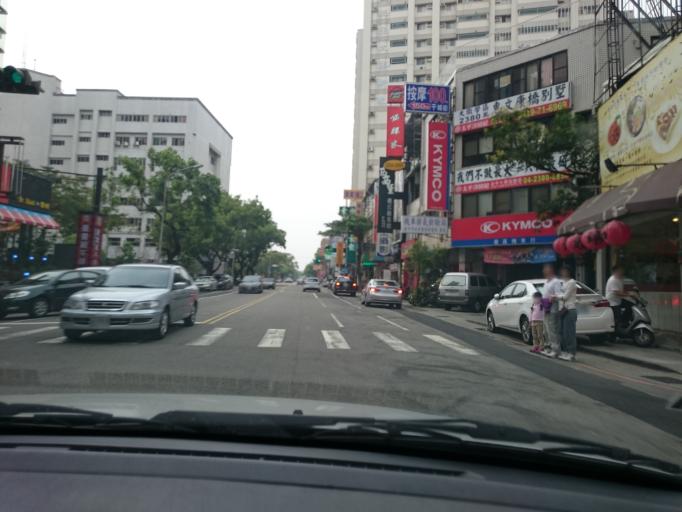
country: TW
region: Taiwan
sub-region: Taichung City
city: Taichung
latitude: 24.1527
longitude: 120.6350
